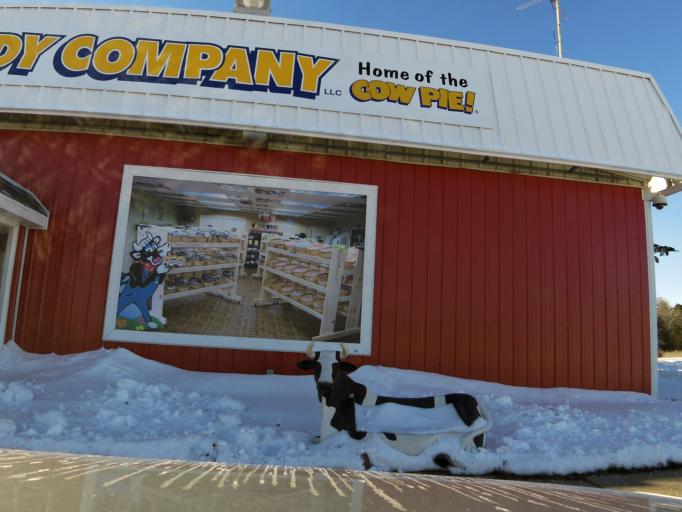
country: US
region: Wisconsin
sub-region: Sauk County
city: West Baraboo
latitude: 43.5247
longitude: -89.7786
